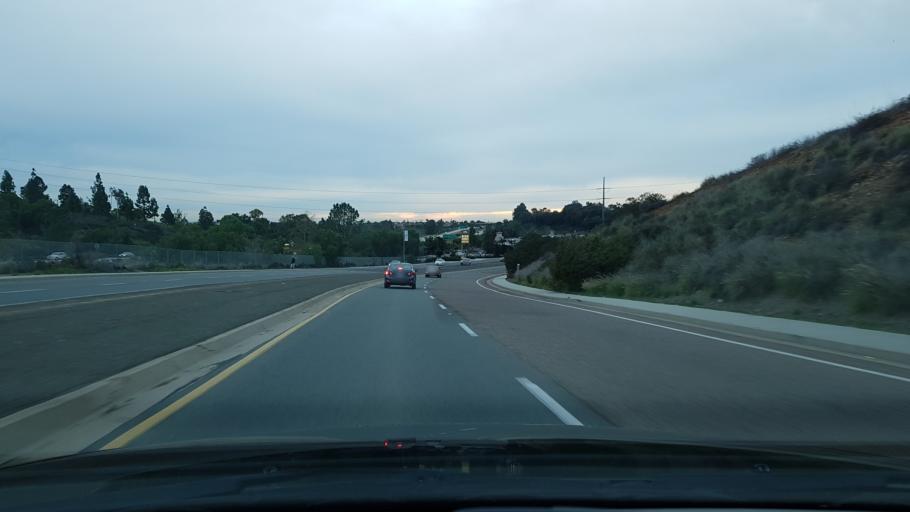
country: US
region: California
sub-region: San Diego County
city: Poway
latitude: 32.9617
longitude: -117.1069
